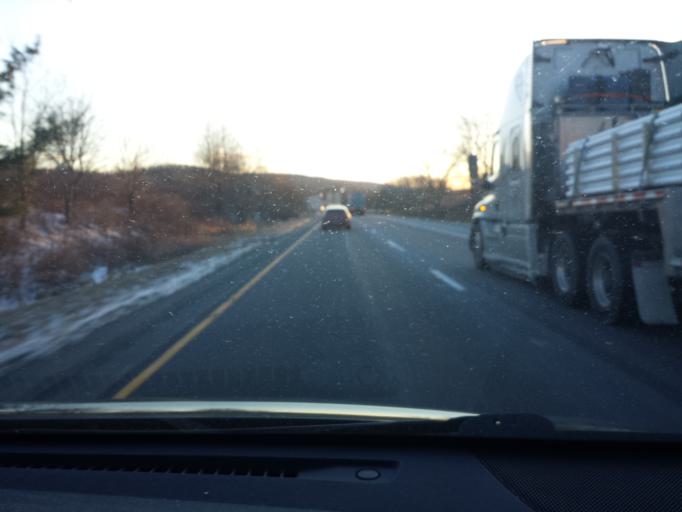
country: US
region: Pennsylvania
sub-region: Centre County
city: Zion
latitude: 40.9775
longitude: -77.6303
